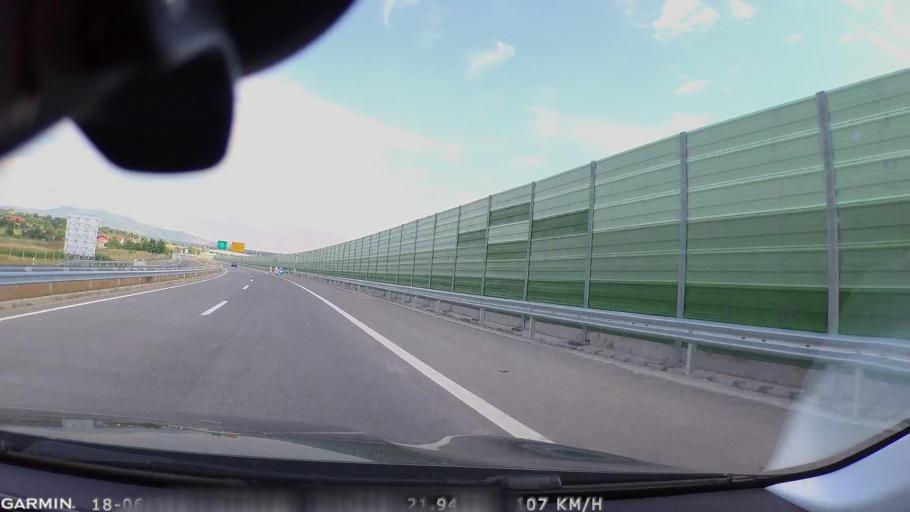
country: MK
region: Sveti Nikole
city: Sveti Nikole
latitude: 41.8735
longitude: 21.9465
